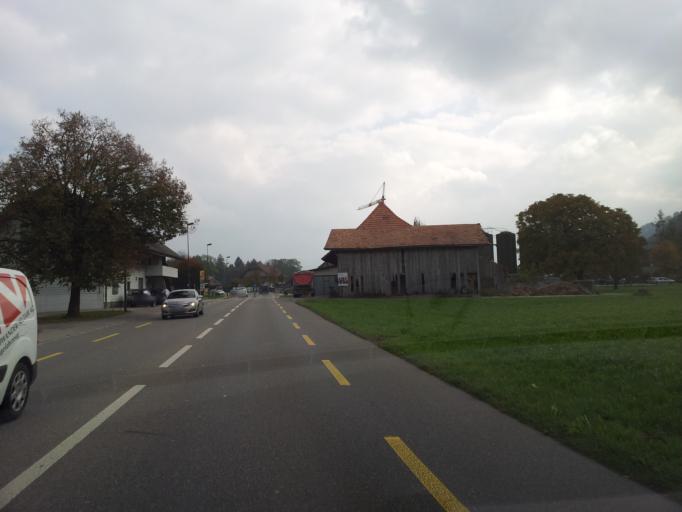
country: CH
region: Bern
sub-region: Bern-Mittelland District
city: Rubigen
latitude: 46.8883
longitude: 7.5241
